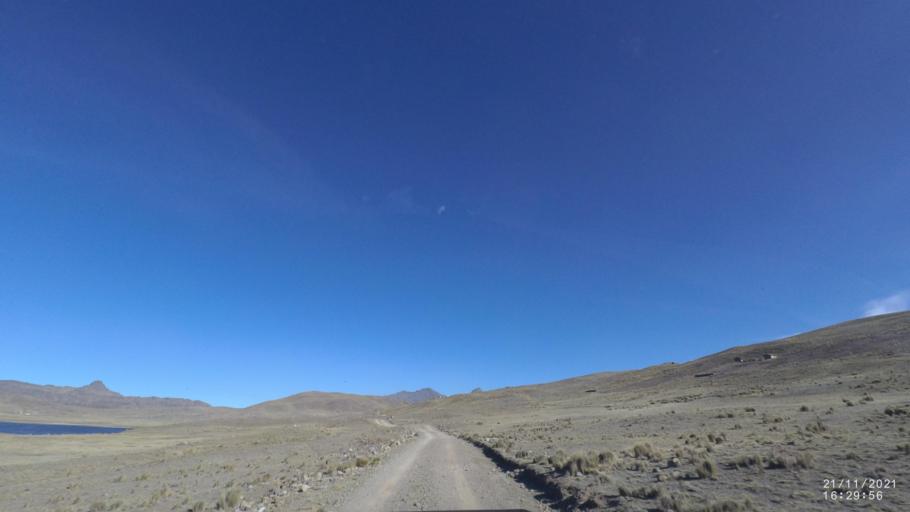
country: BO
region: Cochabamba
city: Cochabamba
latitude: -17.0254
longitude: -66.2829
